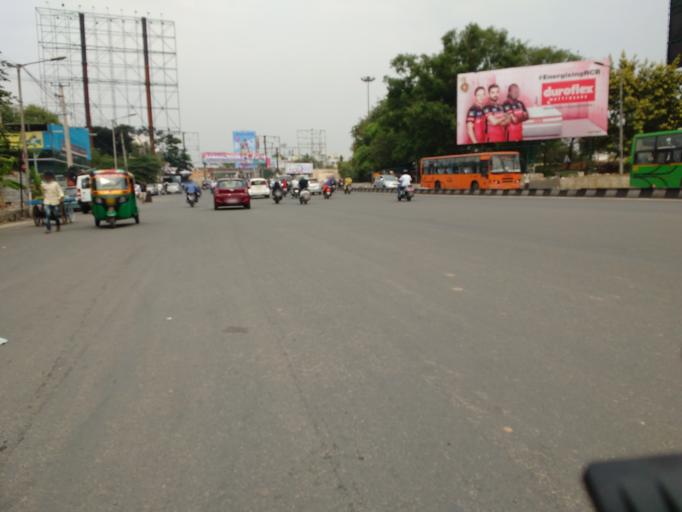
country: IN
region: Karnataka
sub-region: Bangalore Urban
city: Bangalore
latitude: 12.9951
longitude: 77.6658
